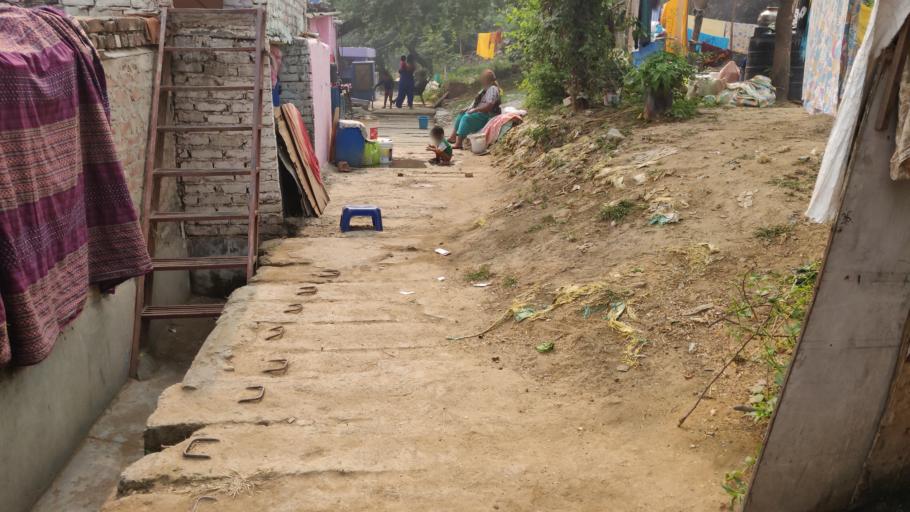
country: IN
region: NCT
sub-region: New Delhi
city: New Delhi
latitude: 28.5691
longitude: 77.2500
